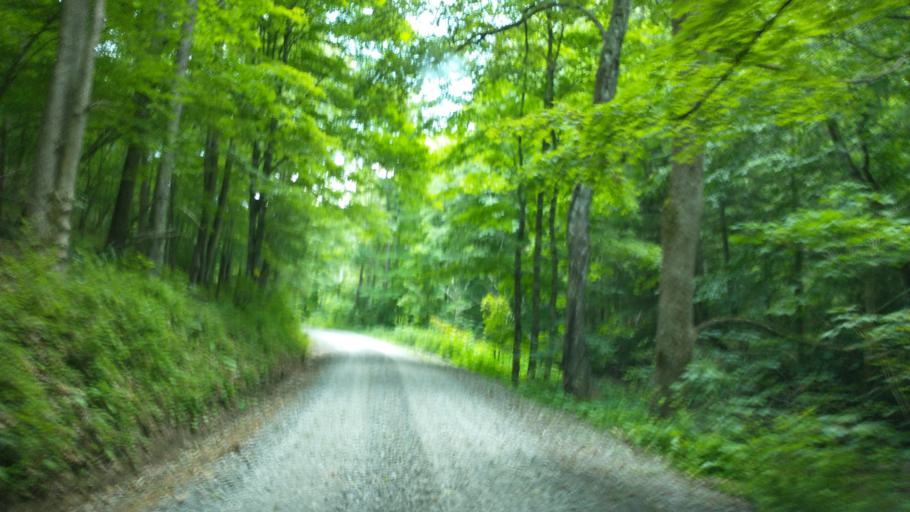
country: US
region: West Virginia
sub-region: Mercer County
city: Athens
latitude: 37.4284
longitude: -80.9970
